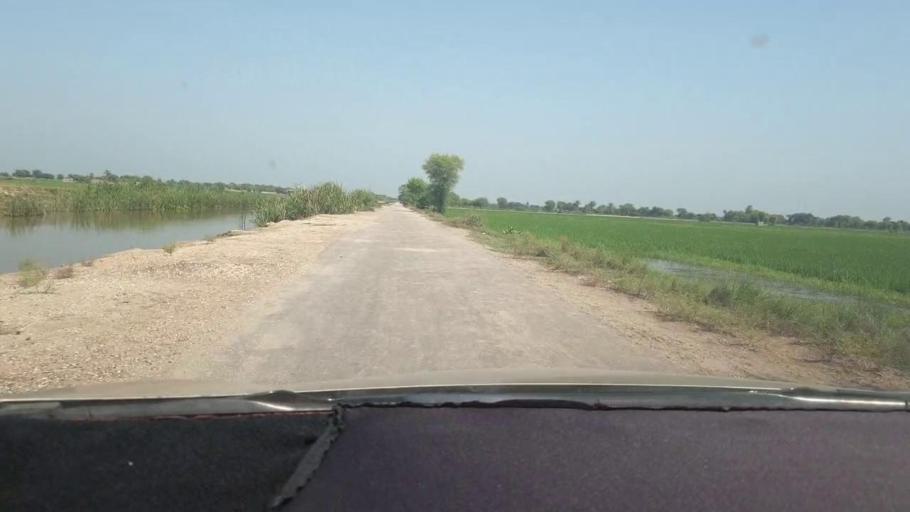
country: PK
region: Sindh
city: Miro Khan
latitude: 27.7058
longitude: 68.0736
